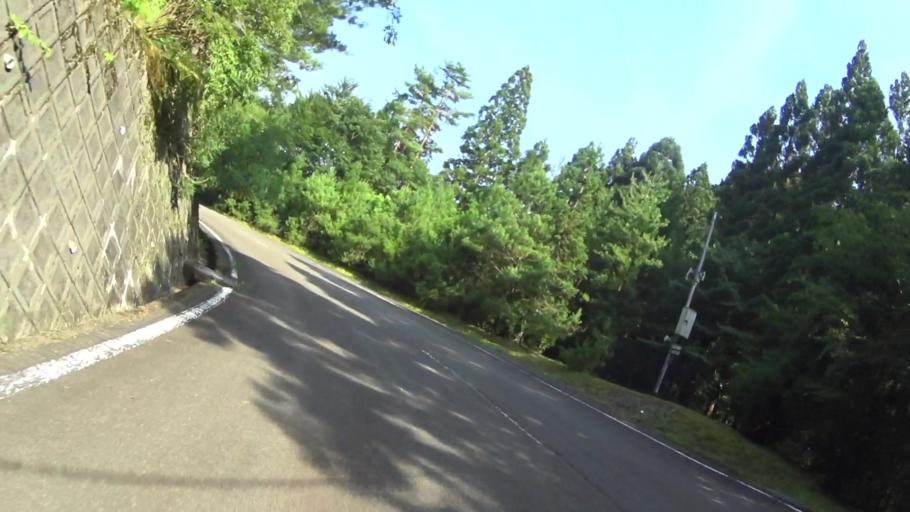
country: JP
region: Fukui
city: Obama
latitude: 35.2730
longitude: 135.6886
